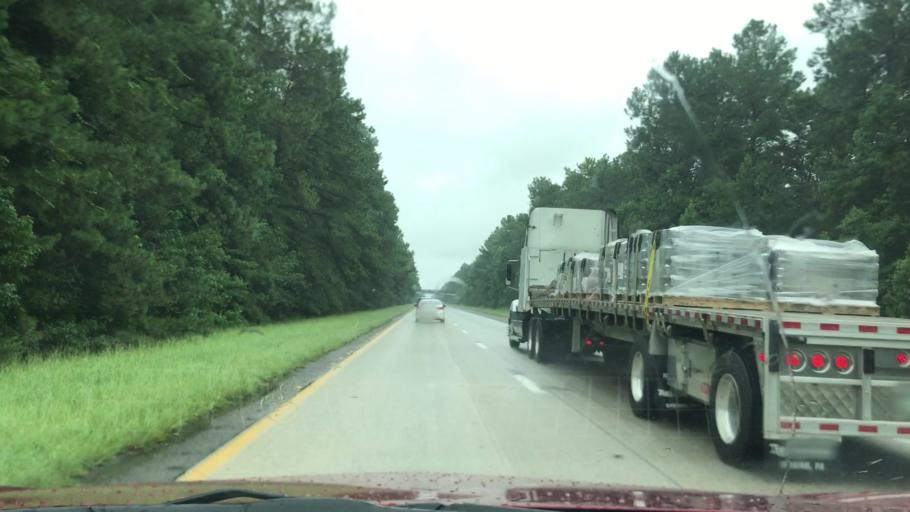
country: US
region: South Carolina
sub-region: Orangeburg County
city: Holly Hill
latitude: 33.2198
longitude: -80.4217
